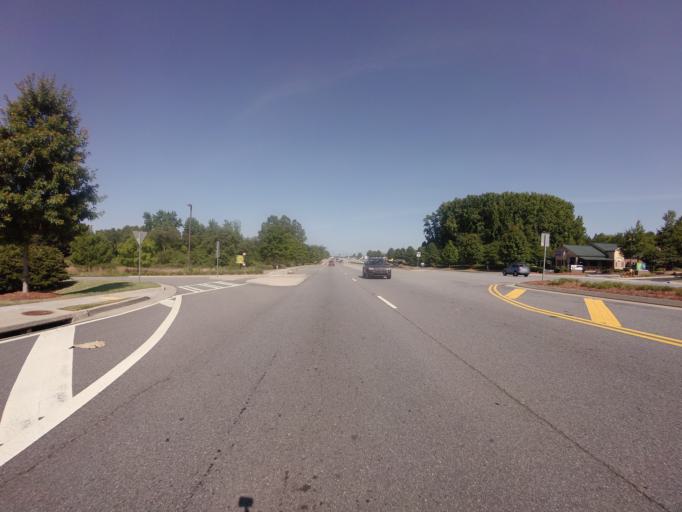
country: US
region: Georgia
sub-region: Fulton County
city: Johns Creek
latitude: 34.0667
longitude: -84.1644
